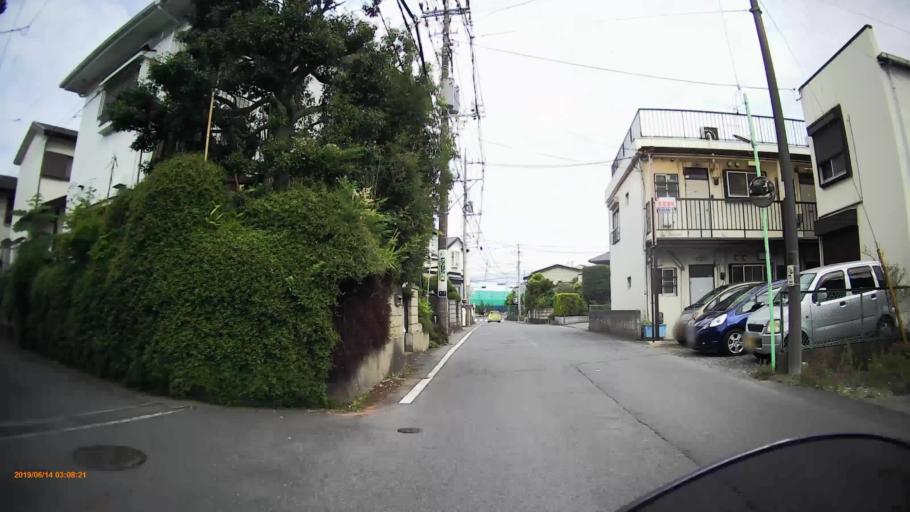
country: JP
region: Kanagawa
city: Fujisawa
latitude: 35.4112
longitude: 139.4583
